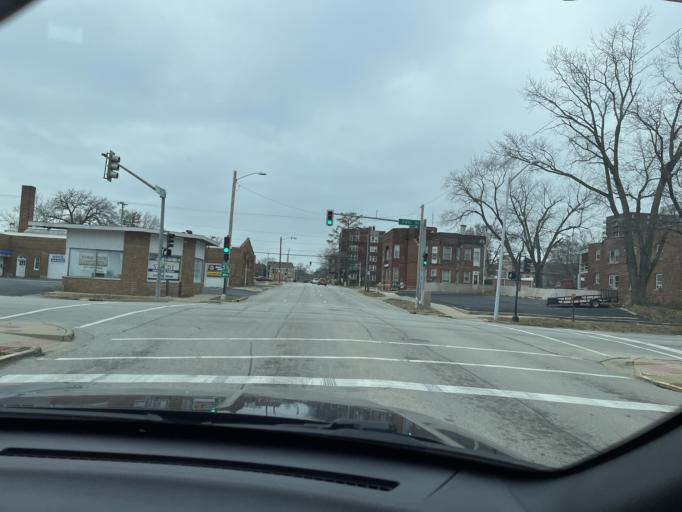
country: US
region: Illinois
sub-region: Sangamon County
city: Springfield
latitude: 39.7949
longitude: -89.6492
